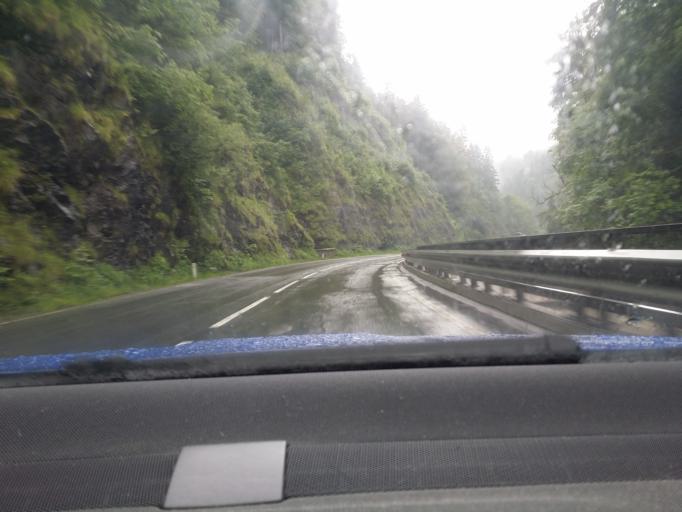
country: AT
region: Salzburg
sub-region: Politischer Bezirk Hallein
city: Abtenau
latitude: 47.5941
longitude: 13.3067
